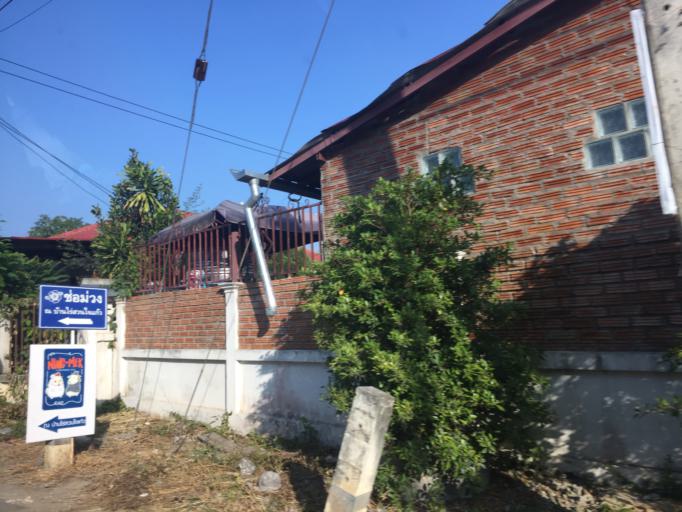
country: TH
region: Chiang Mai
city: Saraphi
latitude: 18.7390
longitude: 99.0097
